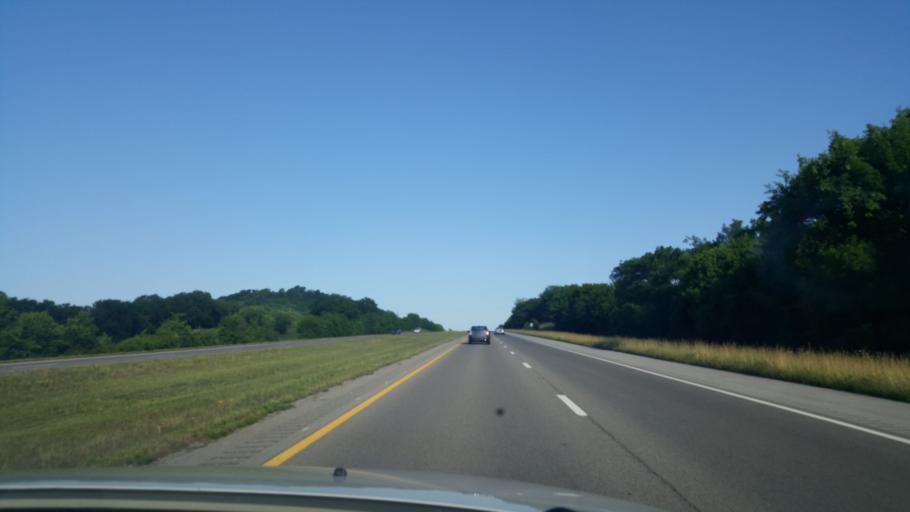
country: US
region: Tennessee
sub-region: Maury County
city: Columbia
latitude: 35.6284
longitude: -87.0884
